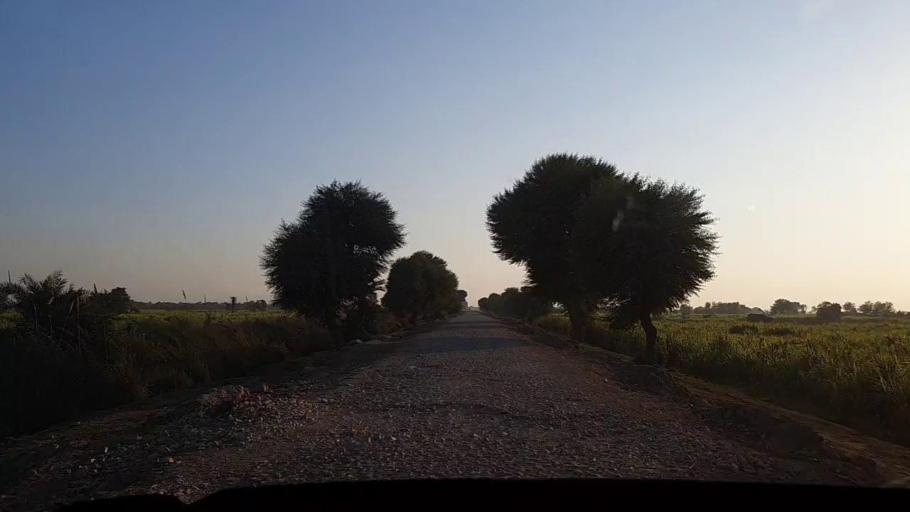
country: PK
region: Sindh
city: Sobhadero
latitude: 27.3769
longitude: 68.3797
